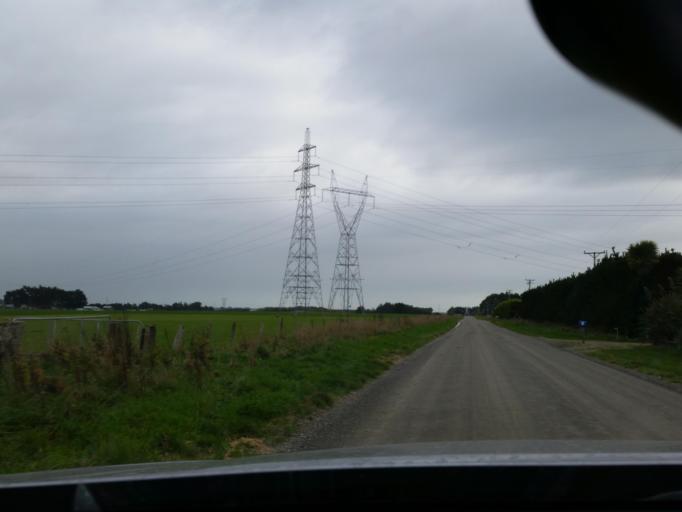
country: NZ
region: Southland
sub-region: Invercargill City
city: Invercargill
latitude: -46.3572
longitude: 168.4287
